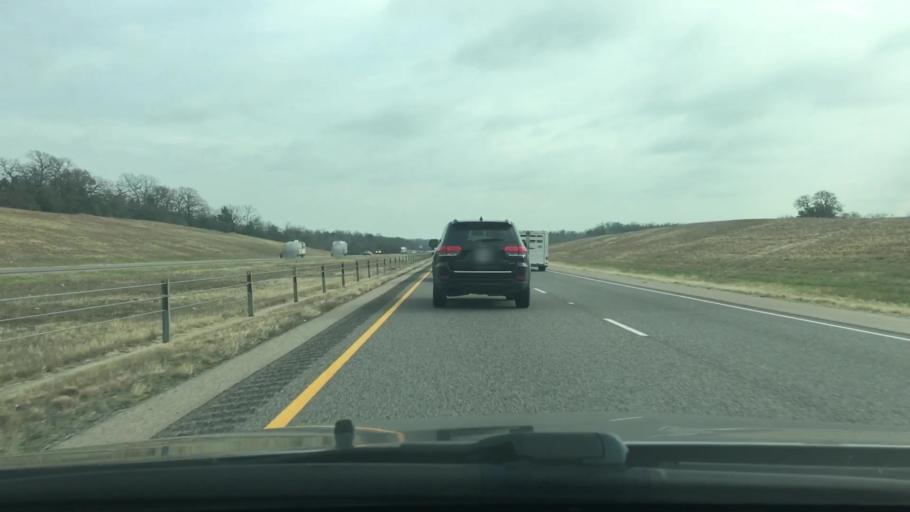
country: US
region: Texas
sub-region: Leon County
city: Buffalo
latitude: 31.5155
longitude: -96.1066
